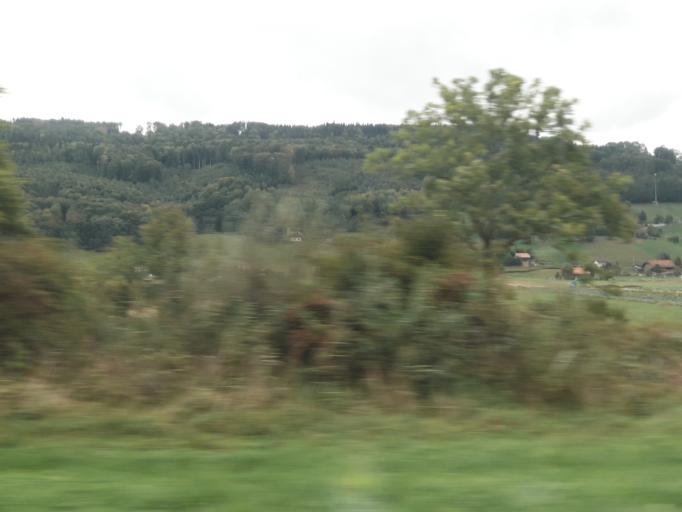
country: CH
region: Bern
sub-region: Bern-Mittelland District
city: Toffen
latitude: 46.8654
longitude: 7.4959
